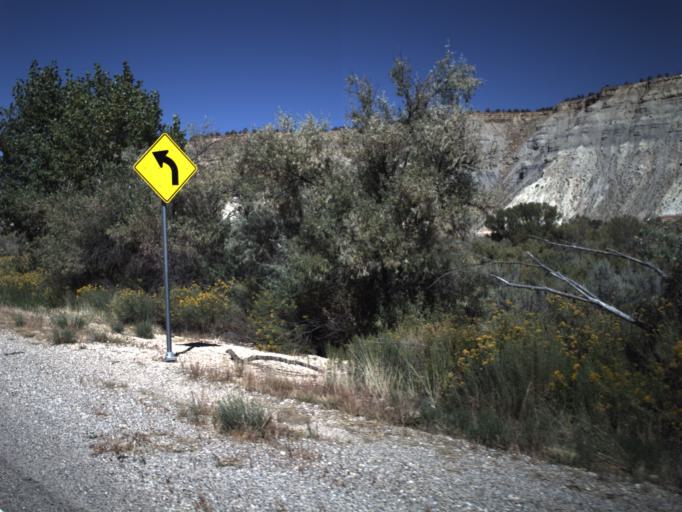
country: US
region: Utah
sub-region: Garfield County
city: Panguitch
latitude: 37.5832
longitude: -112.0571
